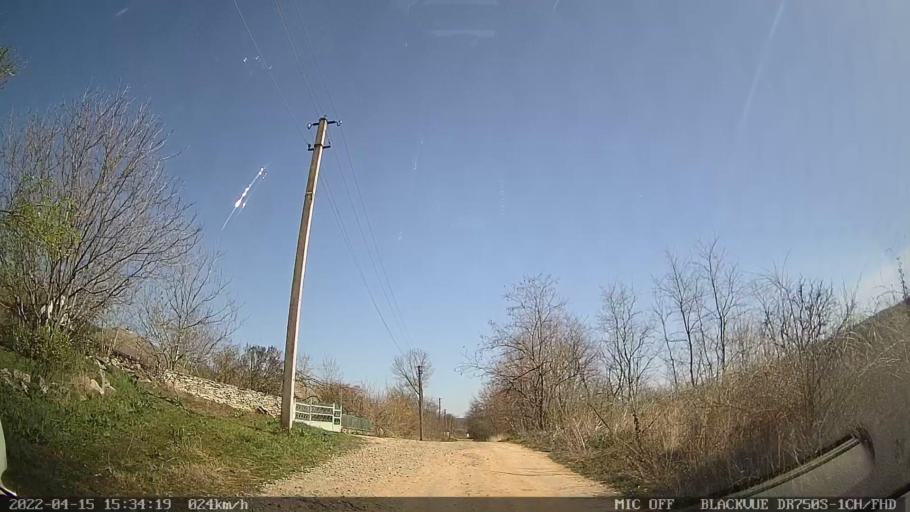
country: MD
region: Raionul Ocnita
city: Otaci
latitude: 48.3477
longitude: 27.9267
